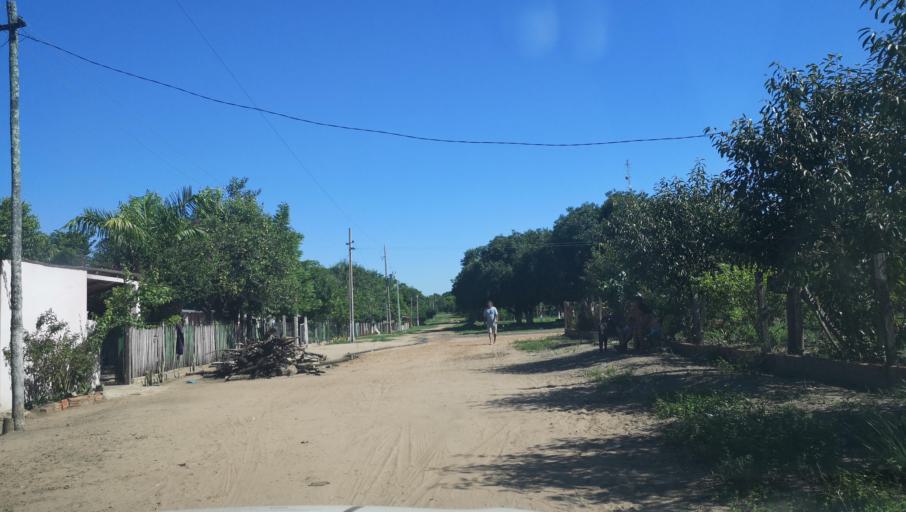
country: PY
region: Caaguazu
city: Carayao
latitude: -25.2043
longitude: -56.3957
